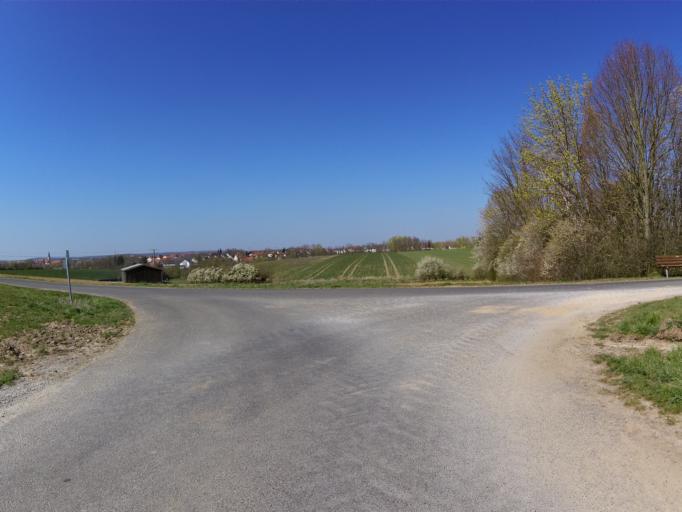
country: DE
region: Bavaria
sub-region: Regierungsbezirk Unterfranken
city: Kurnach
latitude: 49.8414
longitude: 10.0561
